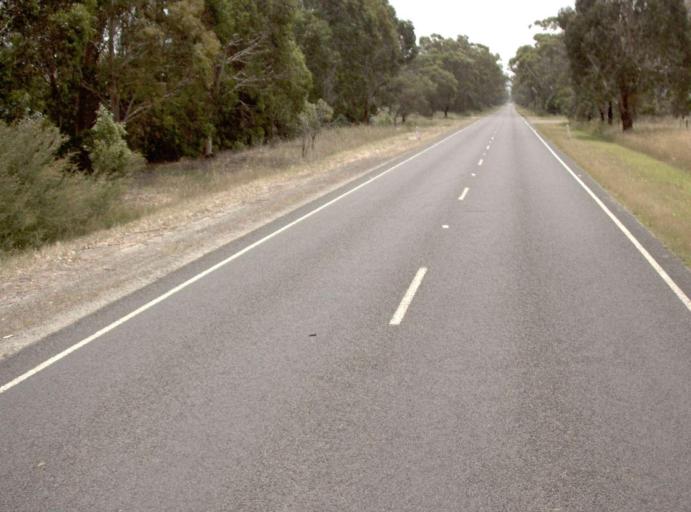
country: AU
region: Victoria
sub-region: Latrobe
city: Traralgon
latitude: -38.4923
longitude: 146.7130
